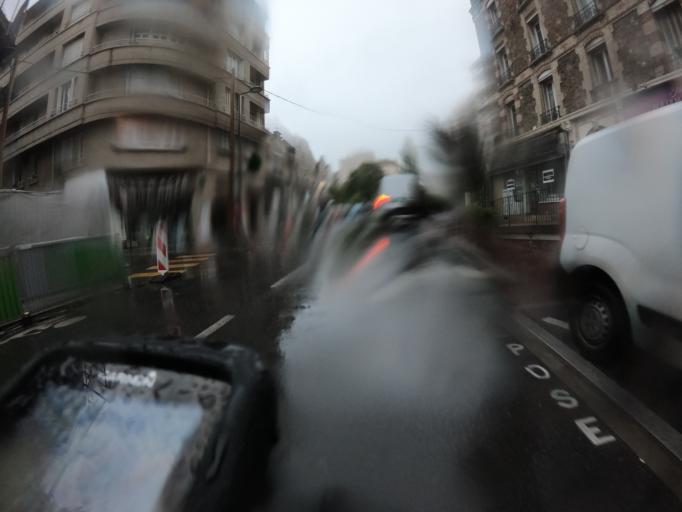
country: FR
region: Ile-de-France
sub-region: Departement des Hauts-de-Seine
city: Vanves
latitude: 48.8190
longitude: 2.2914
